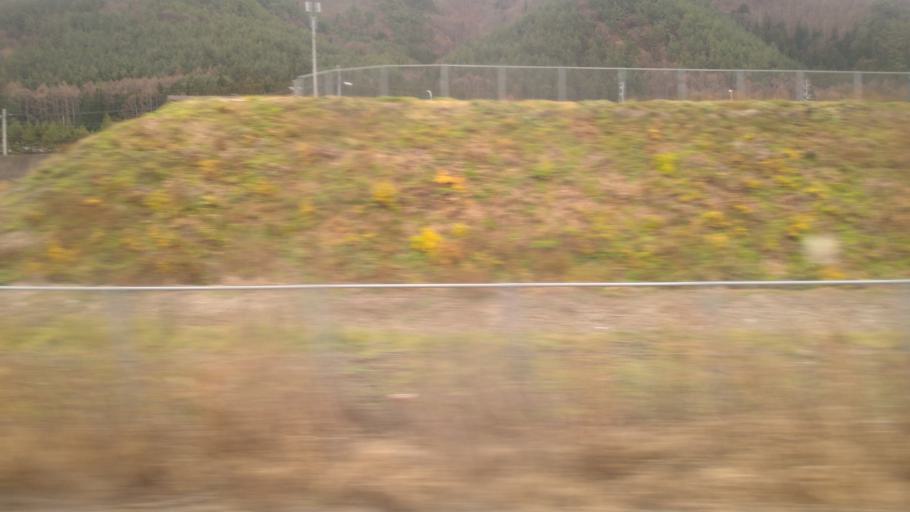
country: JP
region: Nagano
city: Shiojiri
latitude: 36.0694
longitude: 137.9026
